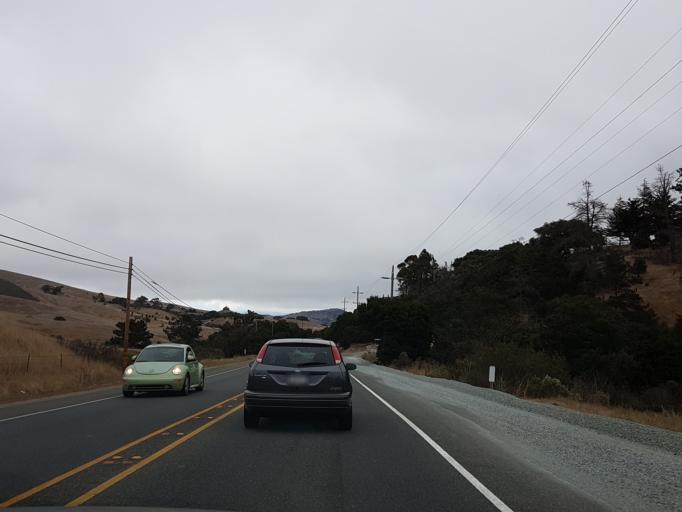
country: US
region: California
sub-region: Monterey County
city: Carmel Valley Village
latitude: 36.5745
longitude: -121.7352
